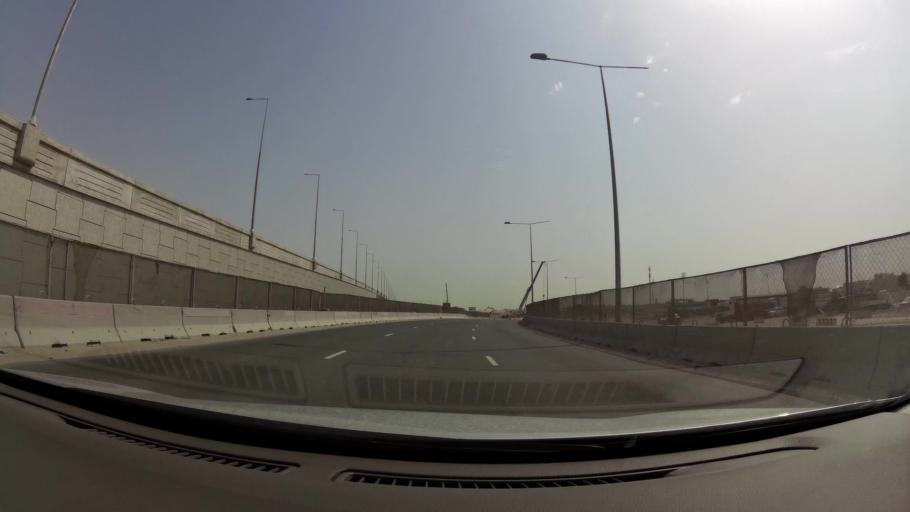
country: QA
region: Al Wakrah
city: Al Wukayr
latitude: 25.1913
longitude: 51.4533
